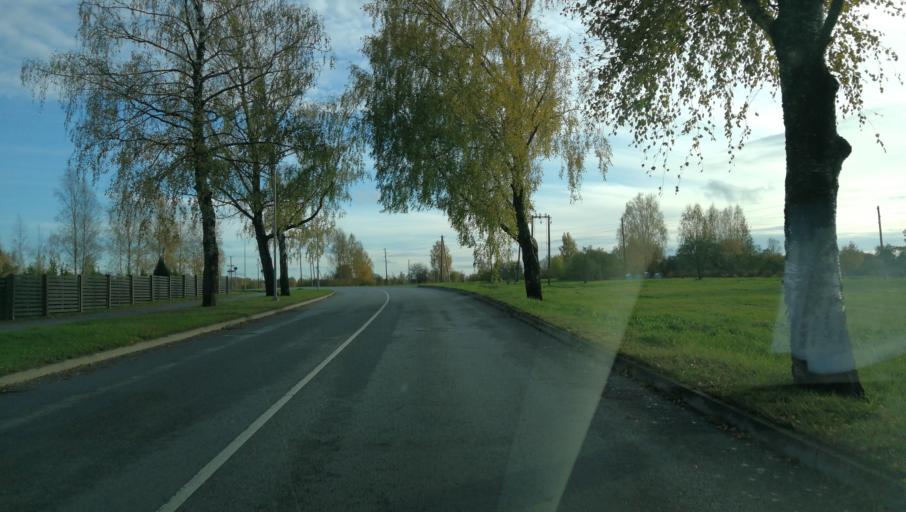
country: LV
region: Cesu Rajons
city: Cesis
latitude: 57.3032
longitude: 25.2428
